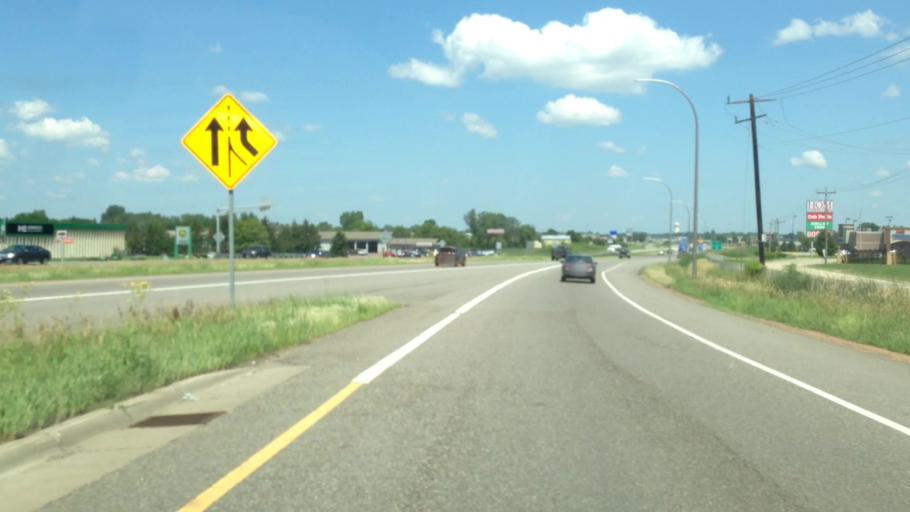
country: US
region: Minnesota
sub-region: Hennepin County
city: Rogers
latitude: 45.2025
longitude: -93.5529
